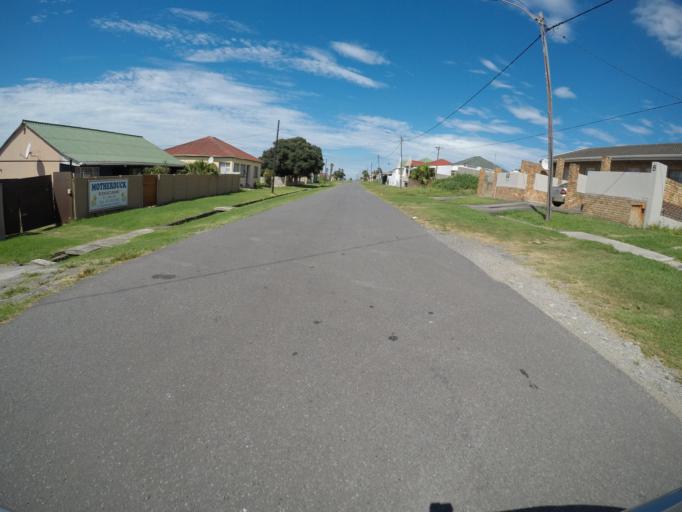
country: ZA
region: Eastern Cape
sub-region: Buffalo City Metropolitan Municipality
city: East London
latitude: -33.0357
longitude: 27.9069
